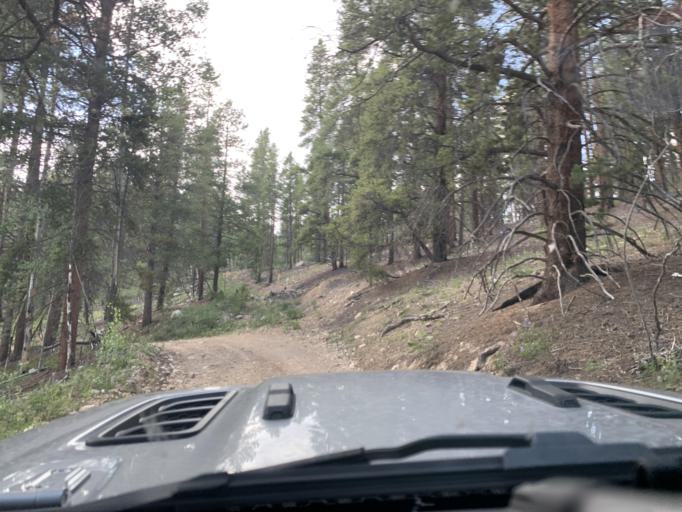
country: US
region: Colorado
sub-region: Lake County
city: Leadville North
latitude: 39.2770
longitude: -106.3116
